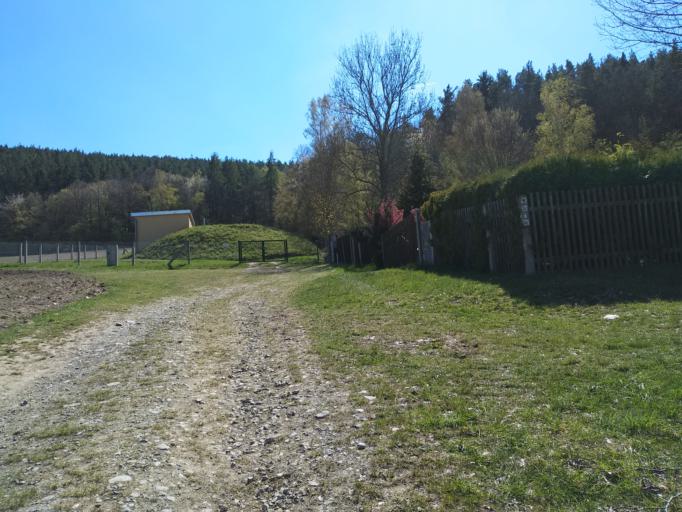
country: DE
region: Thuringia
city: Bad Blankenburg
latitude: 50.6717
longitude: 11.2749
